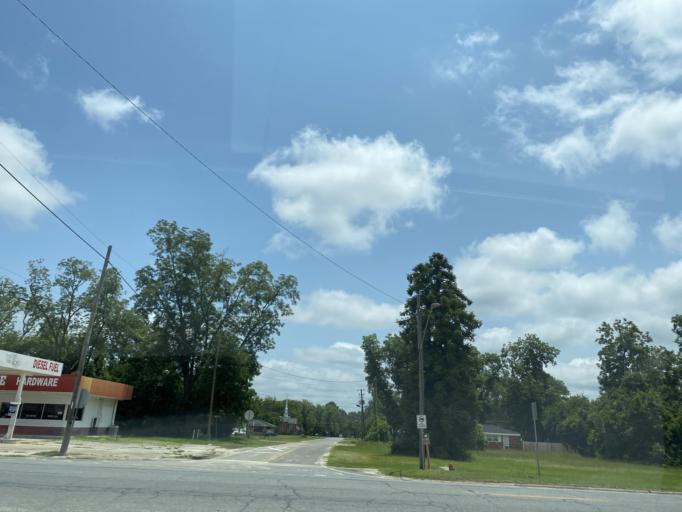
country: US
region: Georgia
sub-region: Wheeler County
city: Alamo
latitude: 32.1465
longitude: -82.7793
